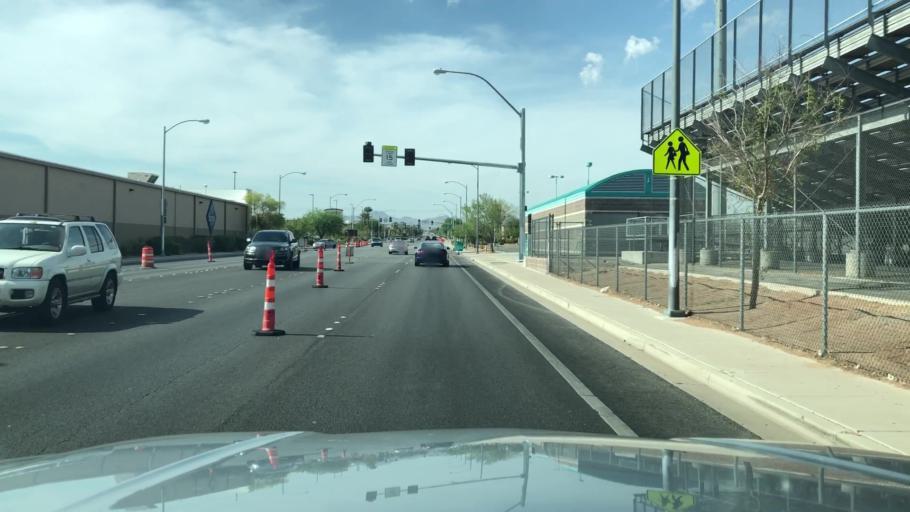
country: US
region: Nevada
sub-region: Clark County
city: Whitney
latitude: 36.0241
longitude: -115.1275
